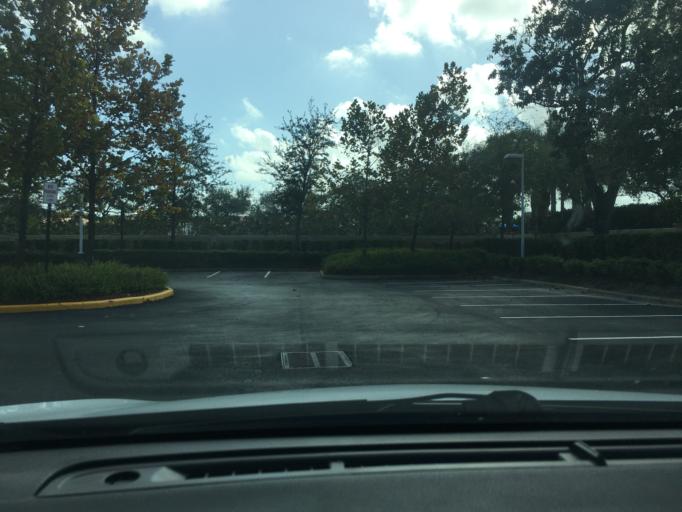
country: US
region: Florida
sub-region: Broward County
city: Dania Beach
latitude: 26.0611
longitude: -80.1694
